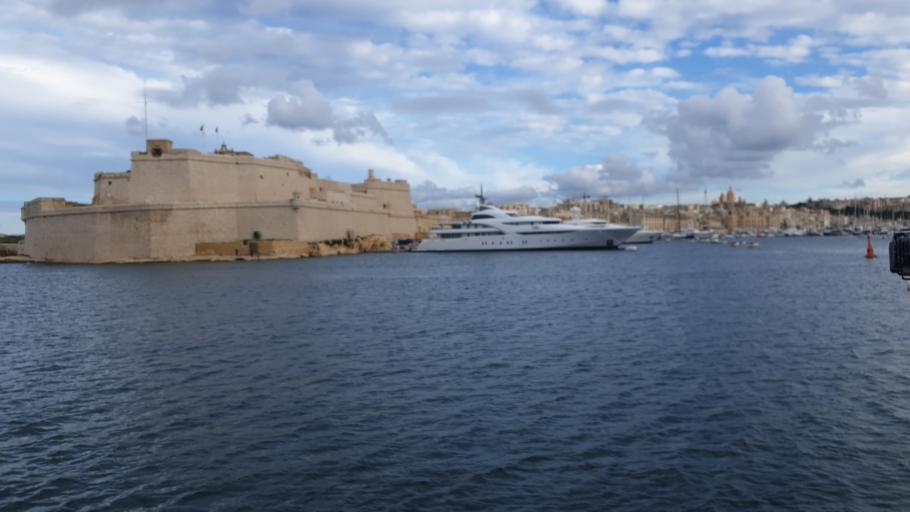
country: MT
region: Il-Birgu
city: Vittoriosa
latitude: 35.8925
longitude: 14.5145
